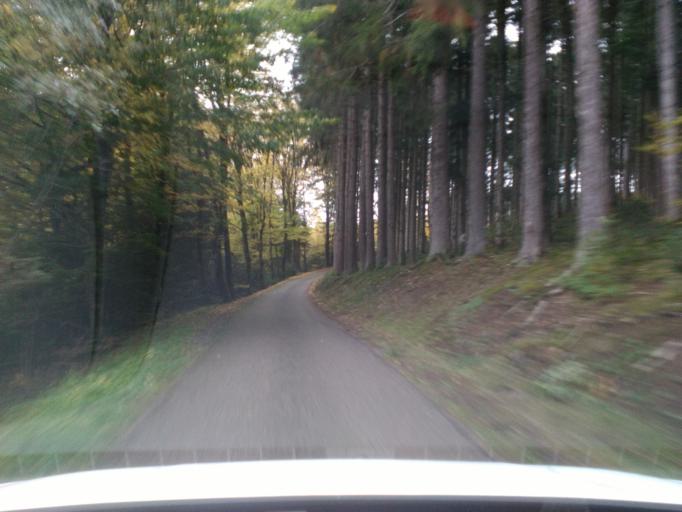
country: FR
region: Lorraine
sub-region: Departement des Vosges
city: Moyenmoutier
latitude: 48.3721
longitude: 6.9011
